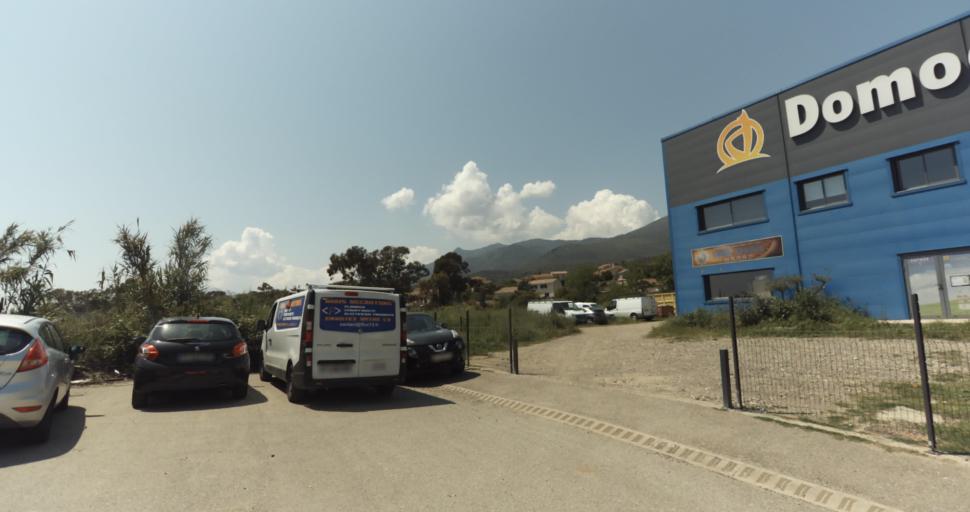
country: FR
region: Corsica
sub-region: Departement de la Haute-Corse
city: Biguglia
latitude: 42.6054
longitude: 9.4349
